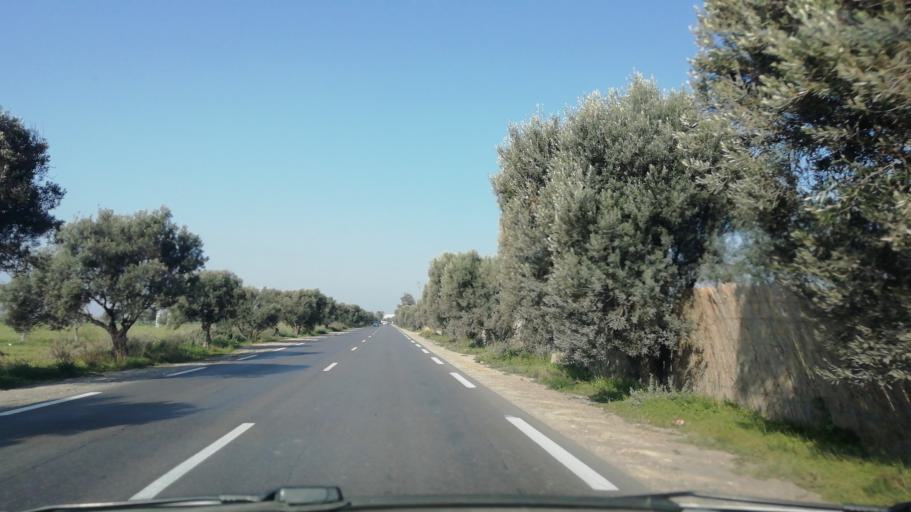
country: DZ
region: Mostaganem
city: Mostaganem
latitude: 35.7418
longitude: -0.0011
